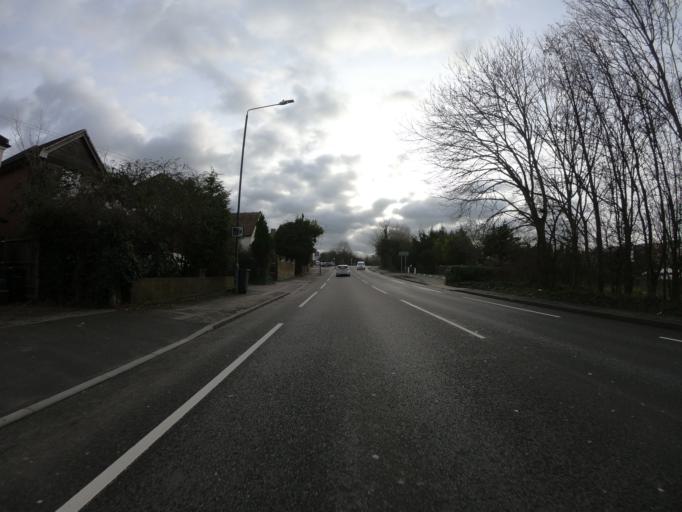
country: GB
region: England
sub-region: Kent
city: Gravesend
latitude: 51.4205
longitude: 0.3610
